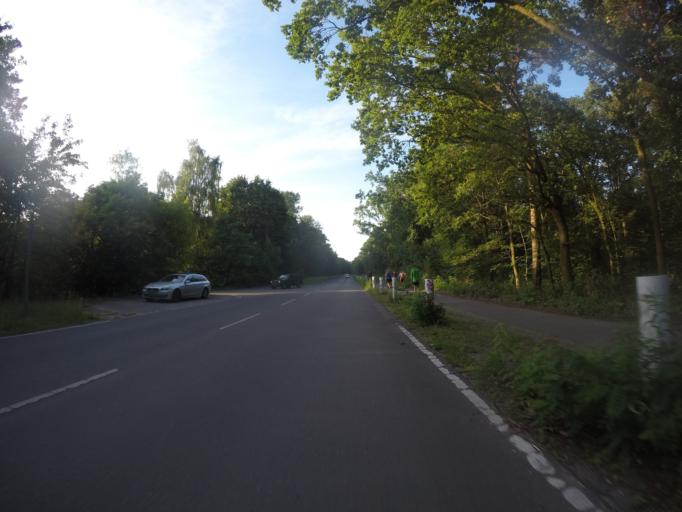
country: DE
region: Berlin
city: Grunewald
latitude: 52.5000
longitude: 13.2506
